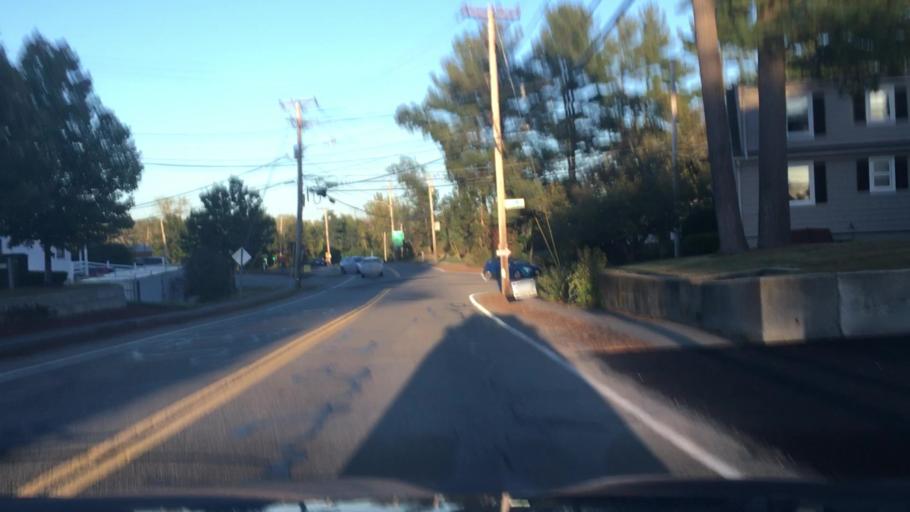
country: US
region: Massachusetts
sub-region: Middlesex County
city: Billerica
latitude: 42.5739
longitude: -71.2837
